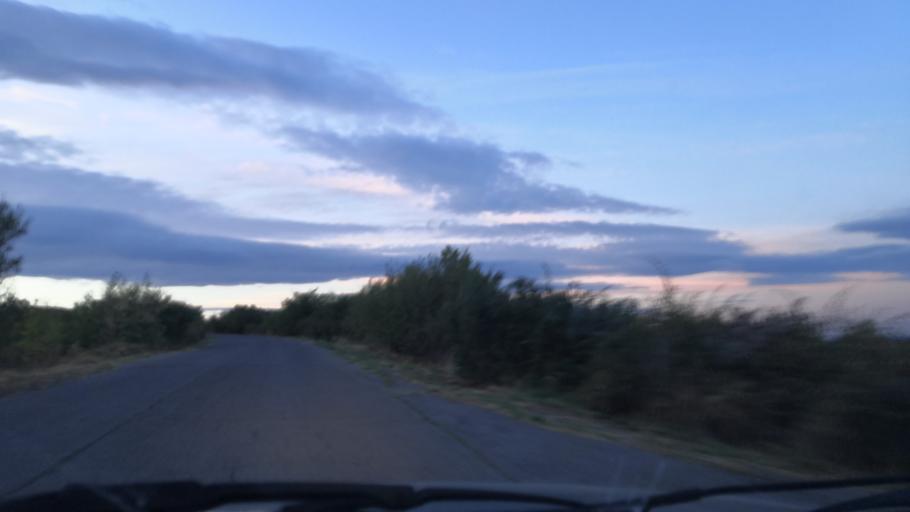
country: RO
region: Mehedinti
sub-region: Comuna Gogosu
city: Balta Verde
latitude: 44.3018
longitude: 22.5528
